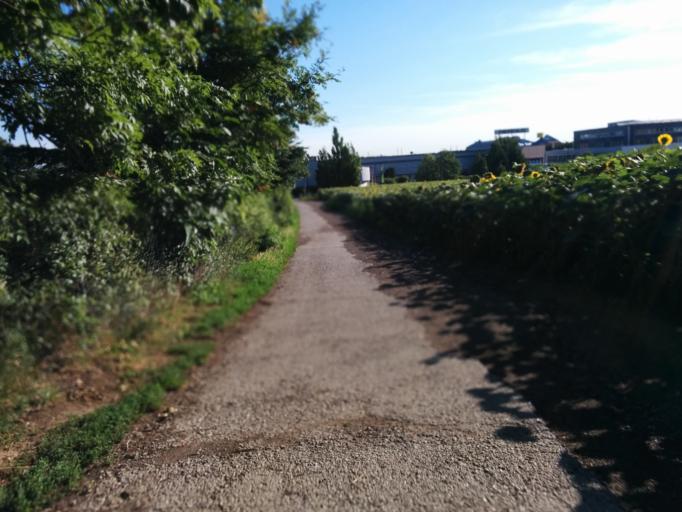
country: AT
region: Lower Austria
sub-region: Politischer Bezirk Modling
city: Neu-Guntramsdorf
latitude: 48.0697
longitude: 16.3017
